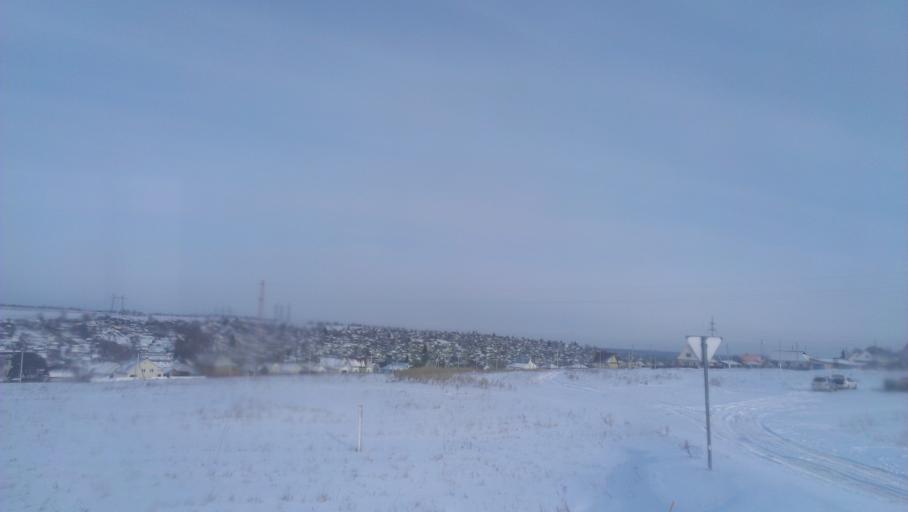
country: RU
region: Altai Krai
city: Gon'ba
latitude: 53.4125
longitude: 83.5573
